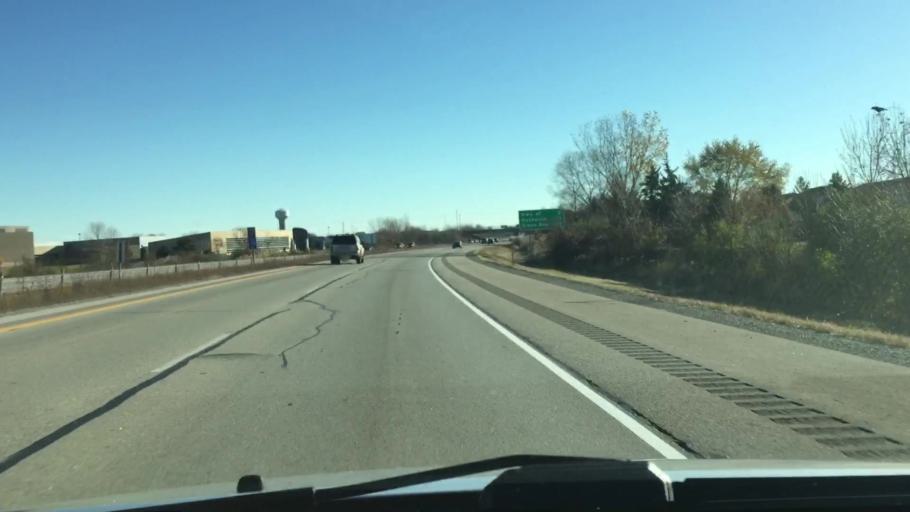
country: US
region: Wisconsin
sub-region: Outagamie County
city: Appleton
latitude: 44.2989
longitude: -88.4539
